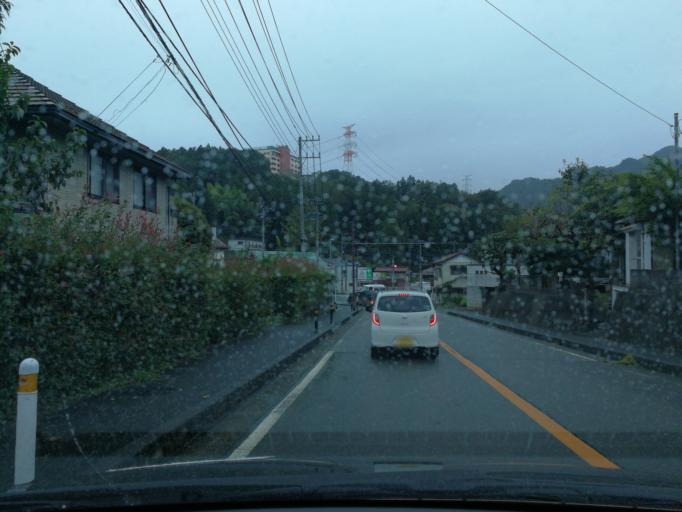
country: JP
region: Yamanashi
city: Uenohara
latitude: 35.6013
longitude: 139.2170
